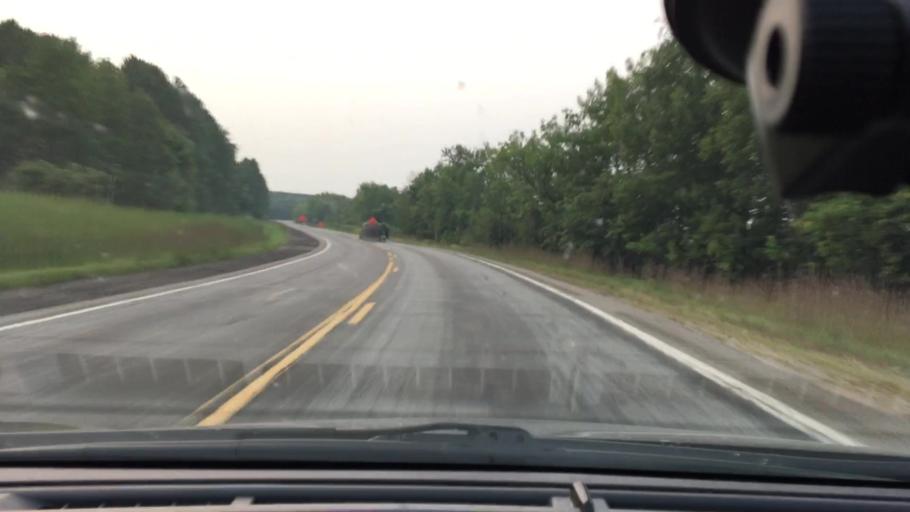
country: US
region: Minnesota
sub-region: Crow Wing County
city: Cross Lake
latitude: 46.7180
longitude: -93.9541
